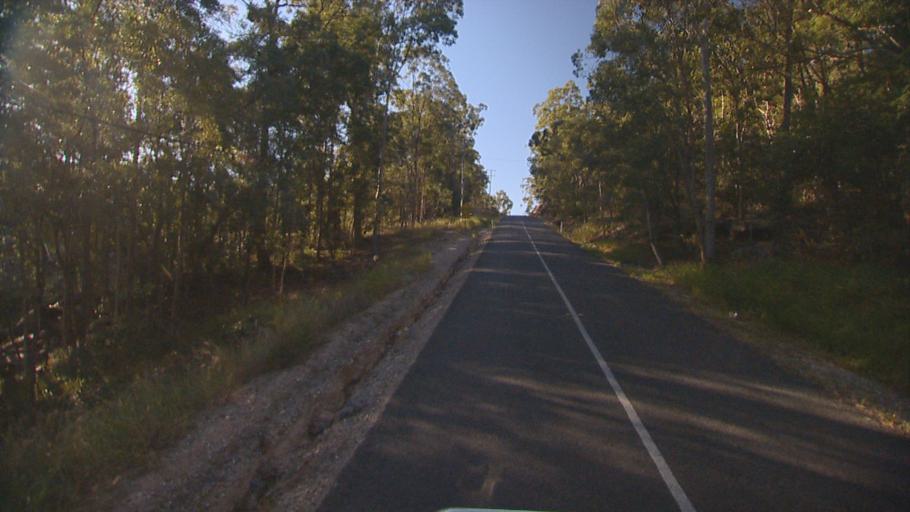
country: AU
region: Queensland
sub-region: Logan
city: Chambers Flat
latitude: -27.7655
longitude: 153.1225
